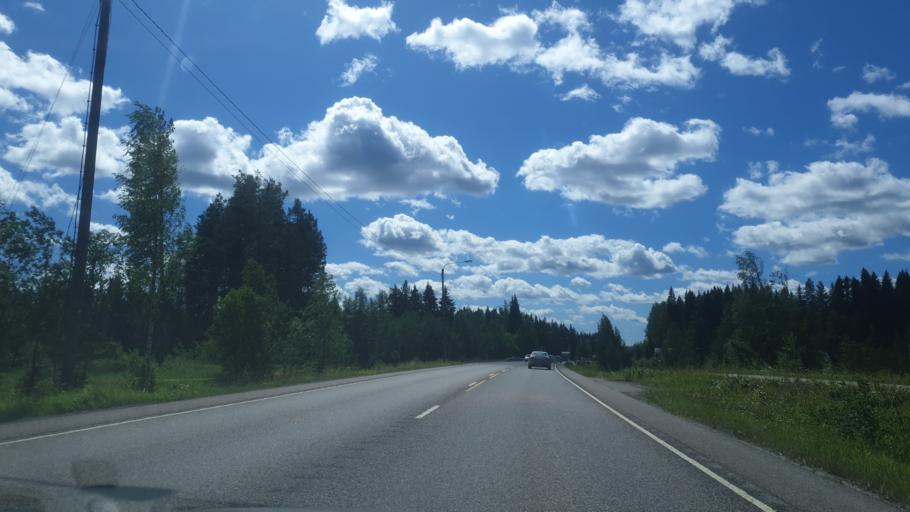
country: FI
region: Northern Savo
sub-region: Varkaus
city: Leppaevirta
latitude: 62.4024
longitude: 27.8249
